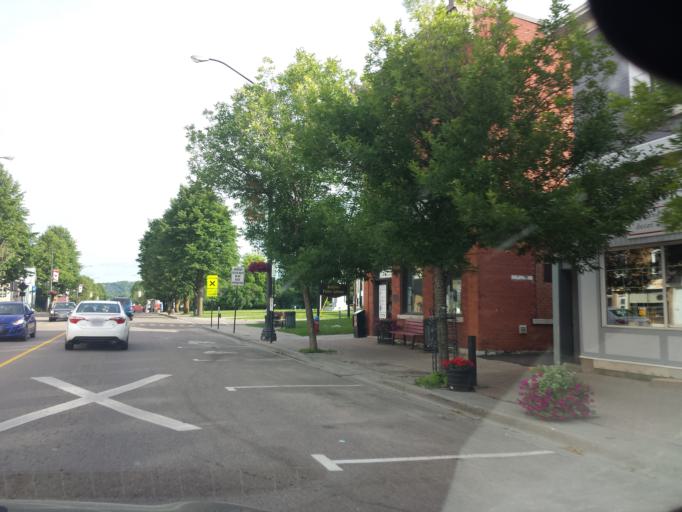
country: CA
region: Ontario
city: Renfrew
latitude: 45.4723
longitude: -76.6845
